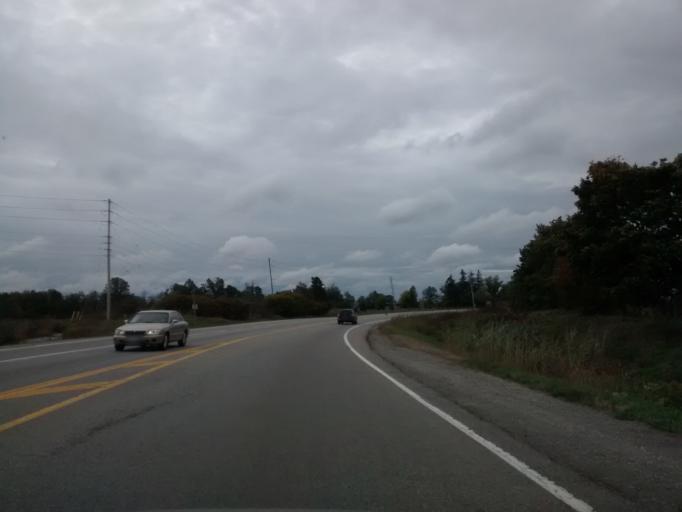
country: CA
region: Ontario
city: Ancaster
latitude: 43.0491
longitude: -79.9744
